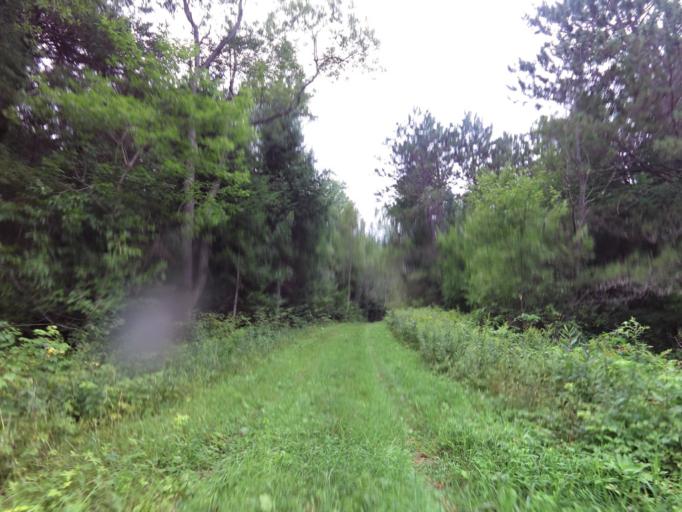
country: CA
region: Quebec
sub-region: Outaouais
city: Wakefield
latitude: 45.6161
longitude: -76.0336
